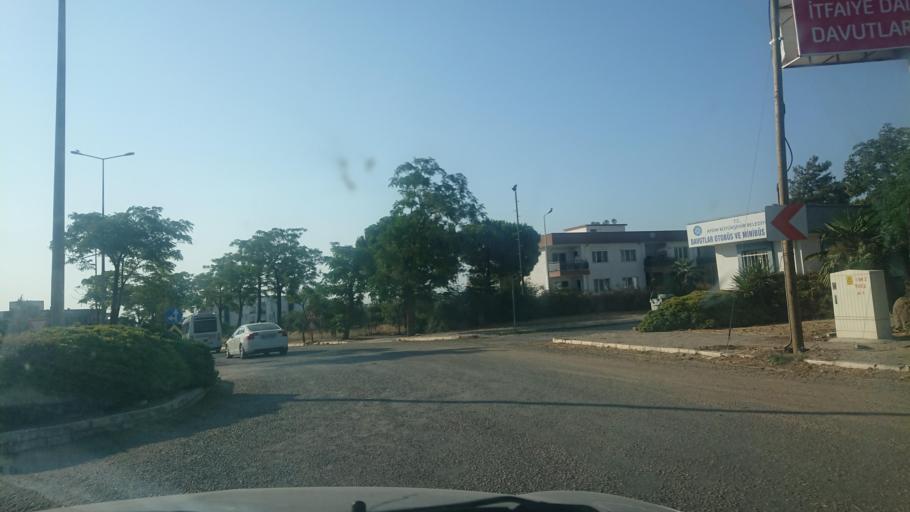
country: TR
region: Aydin
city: Davutlar
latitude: 37.7350
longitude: 27.2841
